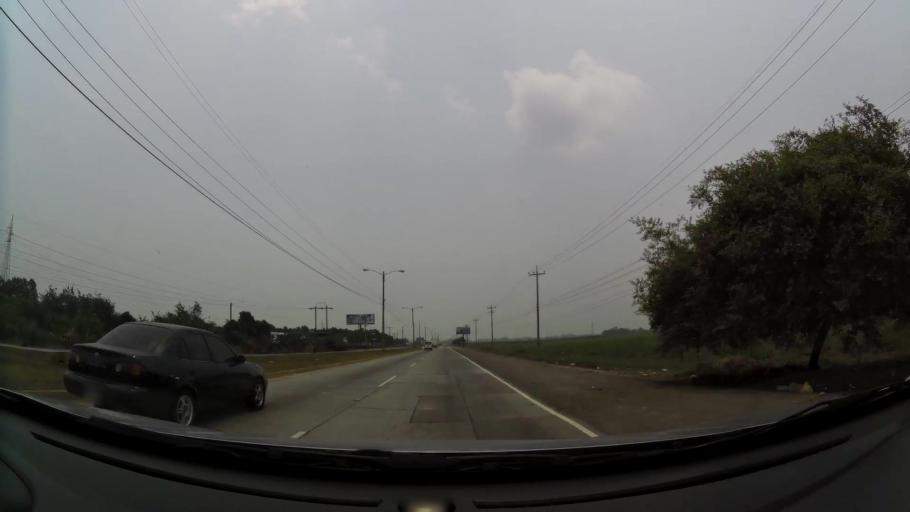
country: HN
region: Cortes
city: La Lima
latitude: 15.4117
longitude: -87.8721
